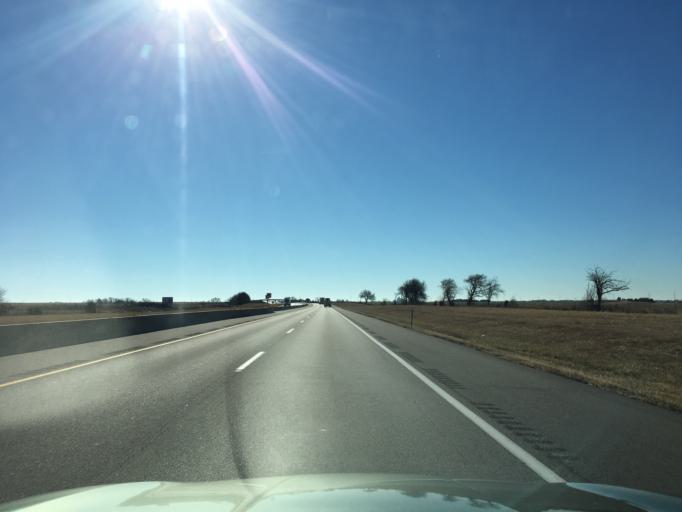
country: US
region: Kansas
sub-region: Sumner County
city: Wellington
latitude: 37.3143
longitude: -97.3401
